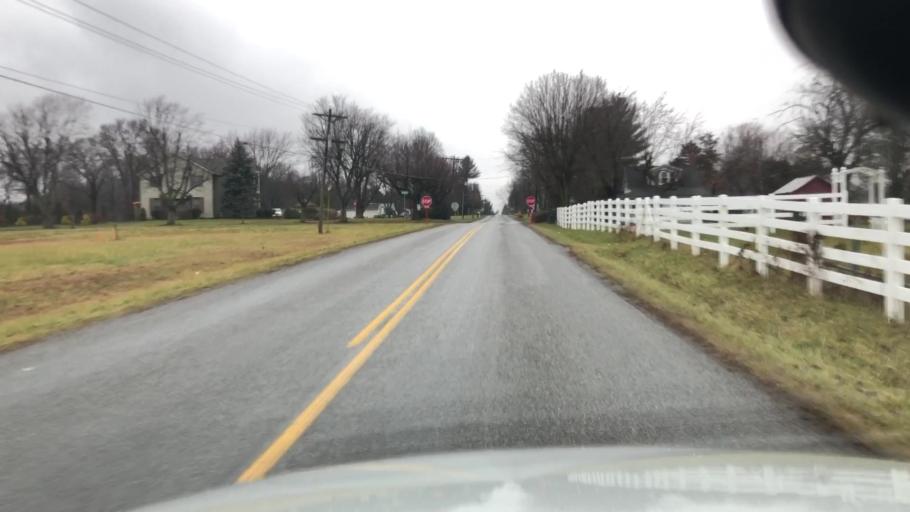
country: US
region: Ohio
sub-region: Allen County
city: Lima
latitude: 40.7702
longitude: -84.0131
